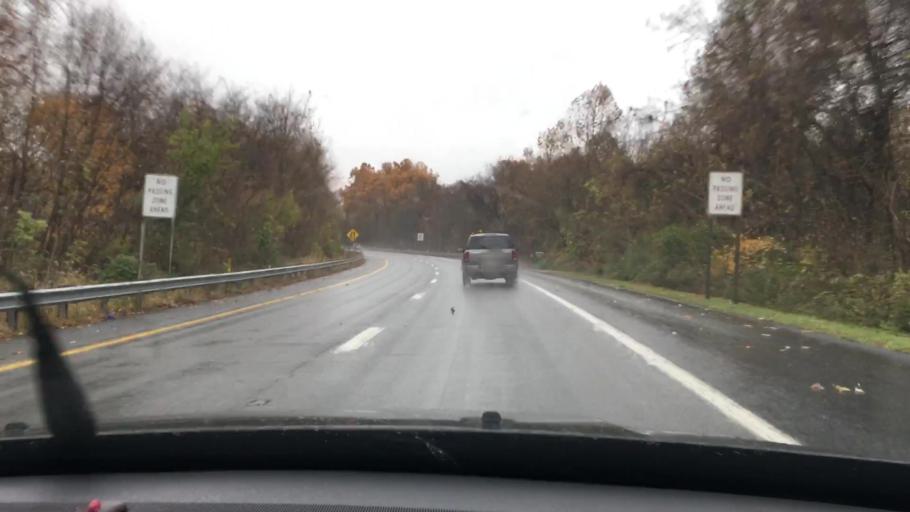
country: US
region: Pennsylvania
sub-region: Lancaster County
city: Willow Street
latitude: 39.9220
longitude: -76.2521
